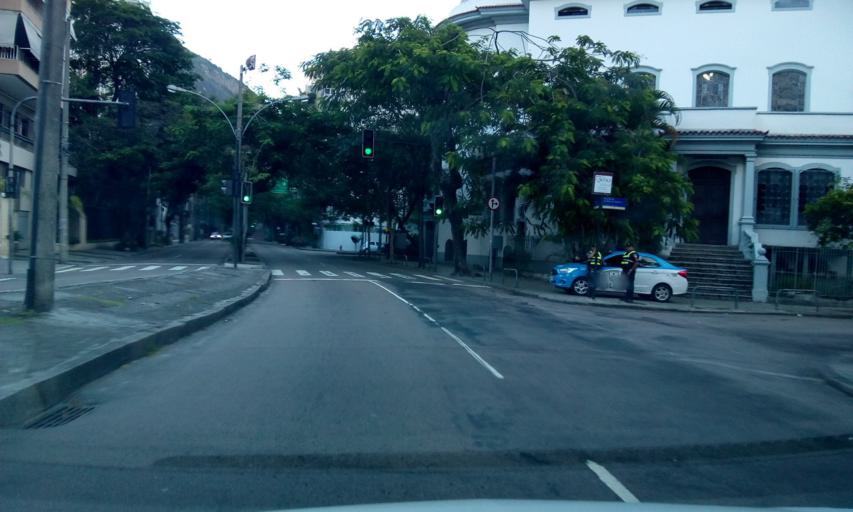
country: BR
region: Rio de Janeiro
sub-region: Rio De Janeiro
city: Rio de Janeiro
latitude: -22.9617
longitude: -43.2031
